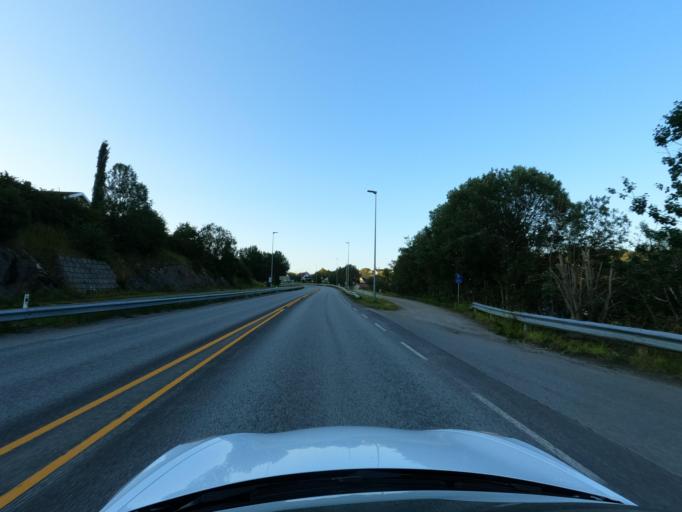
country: NO
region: Troms
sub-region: Harstad
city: Harstad
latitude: 68.7745
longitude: 16.5613
